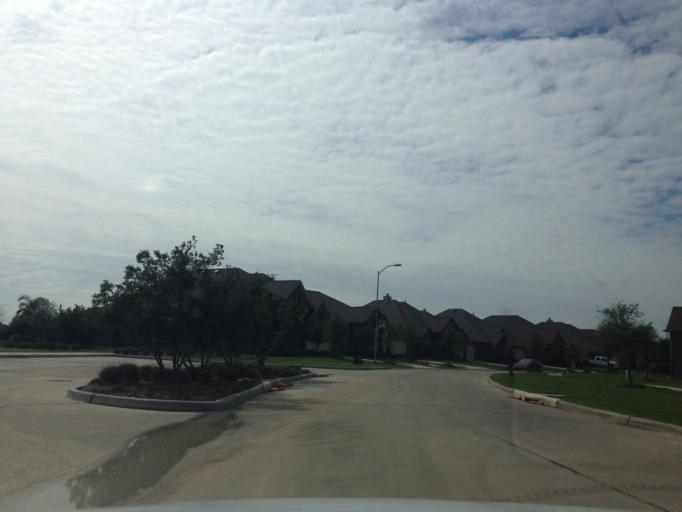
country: US
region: Texas
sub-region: Galveston County
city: Bacliff
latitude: 29.5179
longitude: -95.0148
